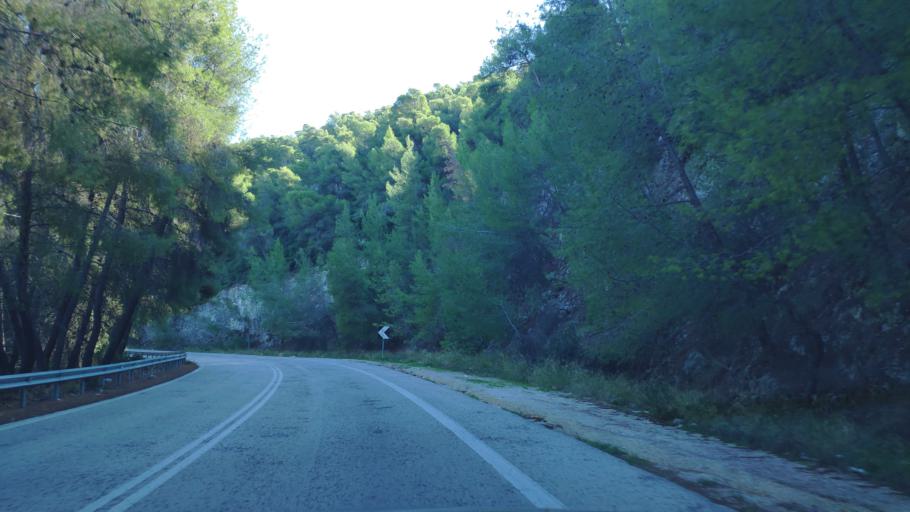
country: GR
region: Peloponnese
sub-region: Nomos Korinthias
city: Sofikon
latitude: 37.8278
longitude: 23.0721
